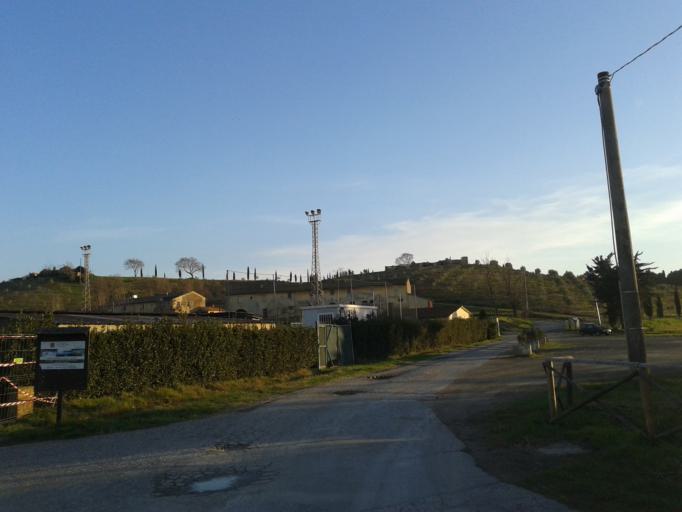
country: IT
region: Tuscany
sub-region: Provincia di Livorno
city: Guasticce
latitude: 43.5927
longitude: 10.4064
